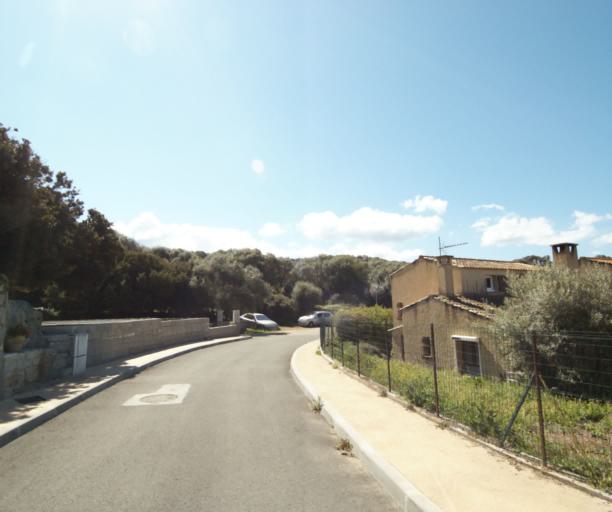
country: FR
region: Corsica
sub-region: Departement de la Corse-du-Sud
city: Propriano
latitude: 41.6754
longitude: 8.9119
